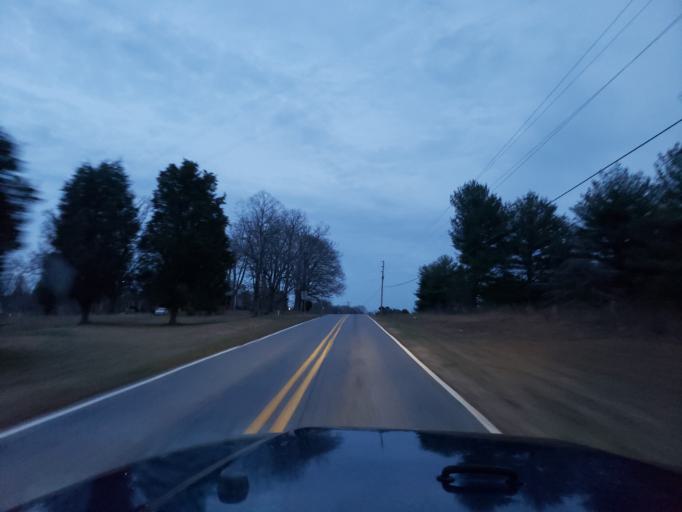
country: US
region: North Carolina
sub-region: Cleveland County
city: White Plains
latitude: 35.1842
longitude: -81.3841
